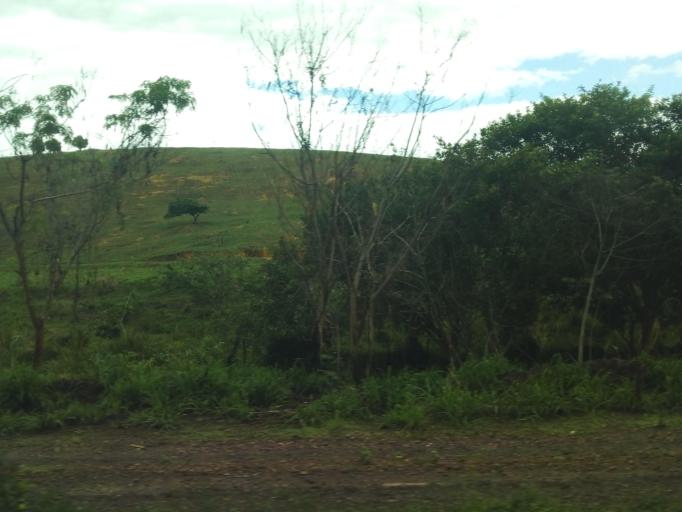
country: BR
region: Minas Gerais
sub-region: Governador Valadares
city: Governador Valadares
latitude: -19.0651
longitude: -42.1495
